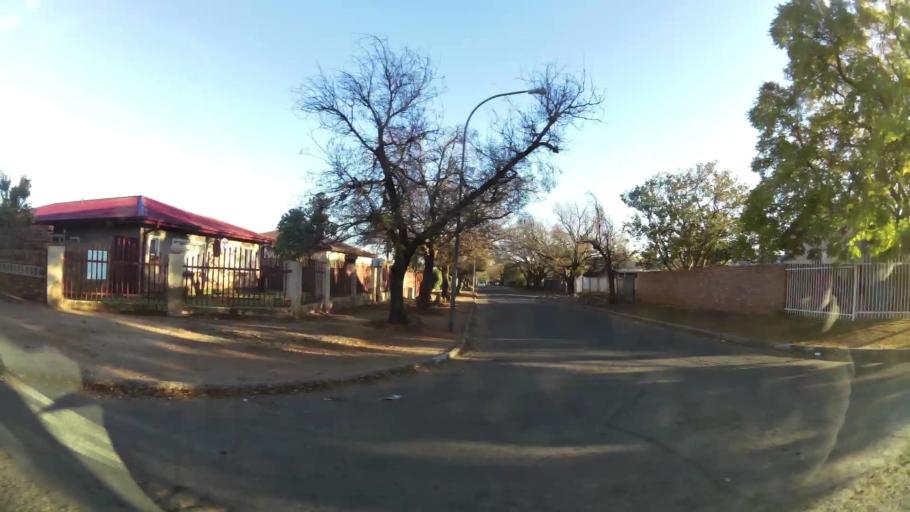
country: ZA
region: Northern Cape
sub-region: Frances Baard District Municipality
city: Kimberley
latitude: -28.7520
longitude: 24.7419
